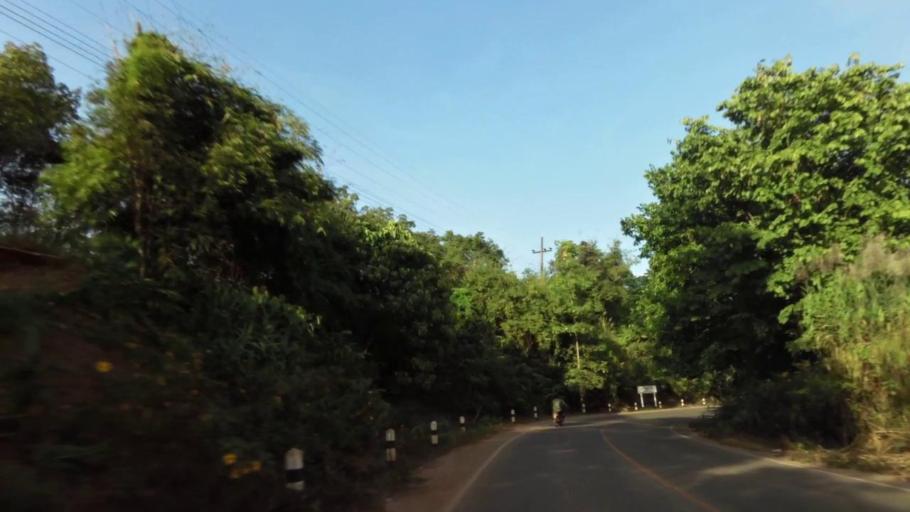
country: TH
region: Chiang Rai
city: Khun Tan
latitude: 19.8599
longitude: 100.3930
